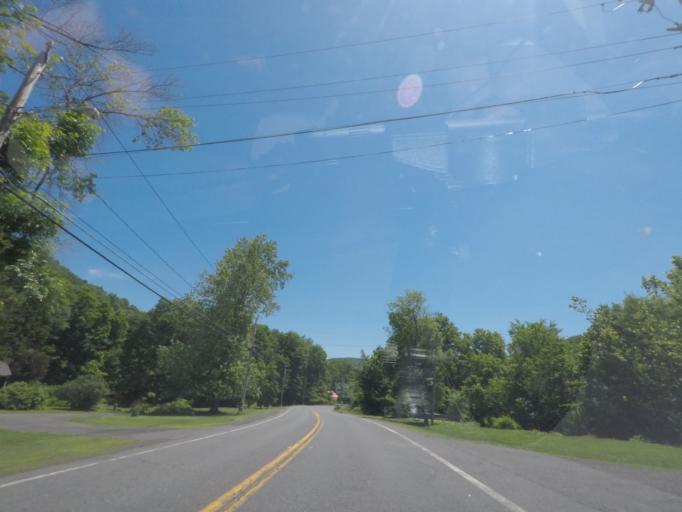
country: US
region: Massachusetts
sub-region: Berkshire County
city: Becket
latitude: 42.2676
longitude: -72.9653
